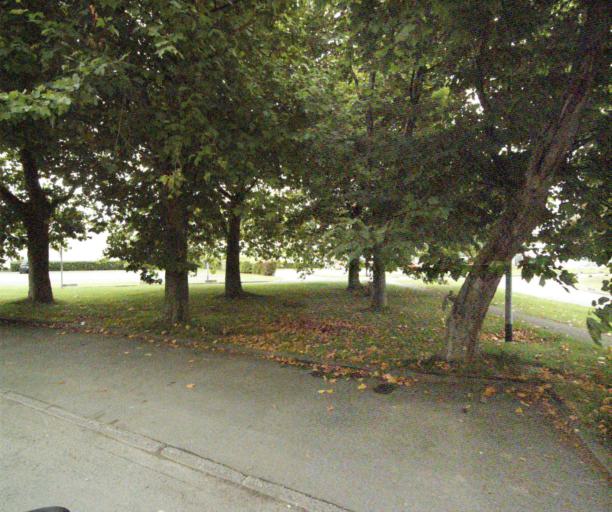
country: FR
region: Nord-Pas-de-Calais
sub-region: Departement du Nord
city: Lezennes
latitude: 50.6162
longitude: 3.1032
